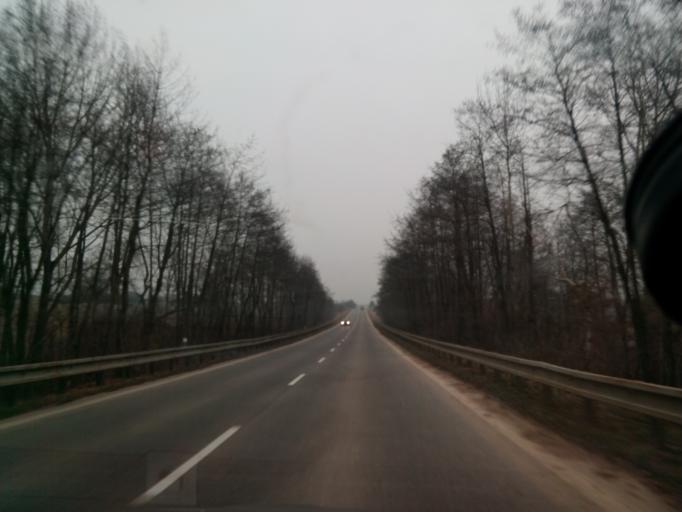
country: SK
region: Kosicky
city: Moldava nad Bodvou
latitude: 48.6872
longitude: 21.0624
